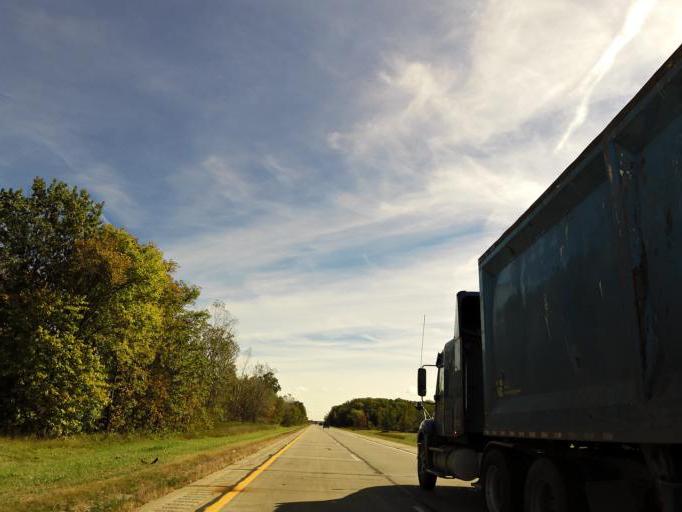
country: US
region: Michigan
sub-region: Macomb County
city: Memphis
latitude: 42.9769
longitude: -82.8211
